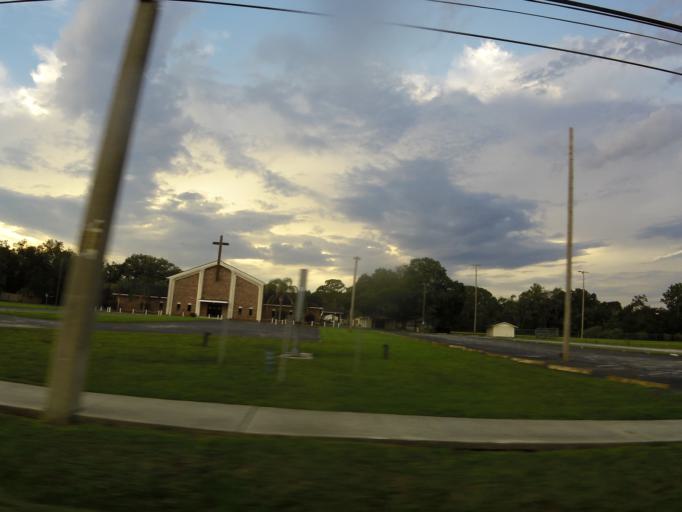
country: US
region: Florida
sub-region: Clay County
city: Bellair-Meadowbrook Terrace
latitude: 30.2740
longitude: -81.7814
